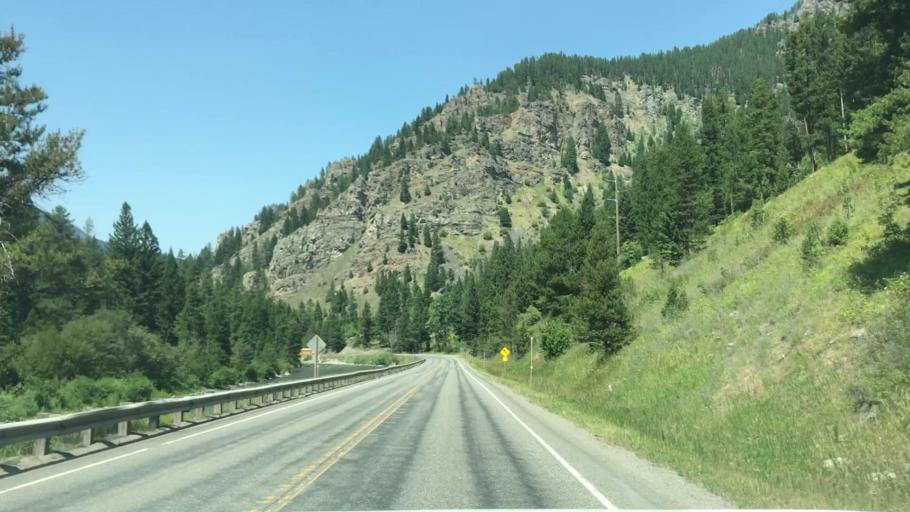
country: US
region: Montana
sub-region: Gallatin County
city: Big Sky
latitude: 45.3924
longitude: -111.2051
